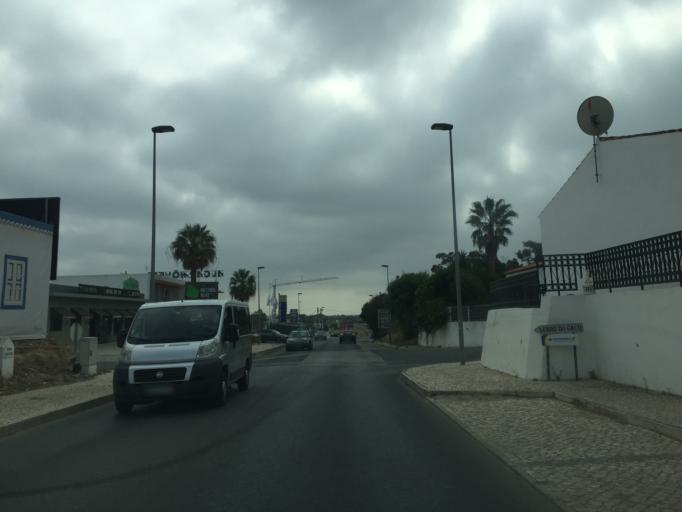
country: PT
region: Faro
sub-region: Loule
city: Almancil
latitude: 37.0842
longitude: -8.0192
